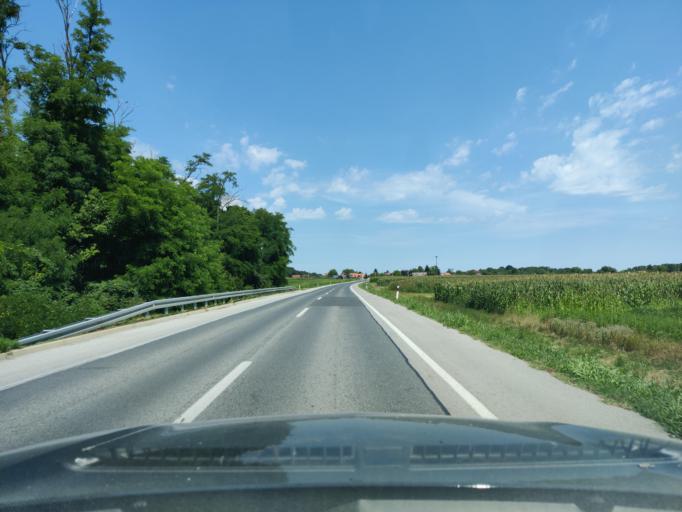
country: HR
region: Medimurska
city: Senkovec
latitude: 46.4183
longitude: 16.4253
